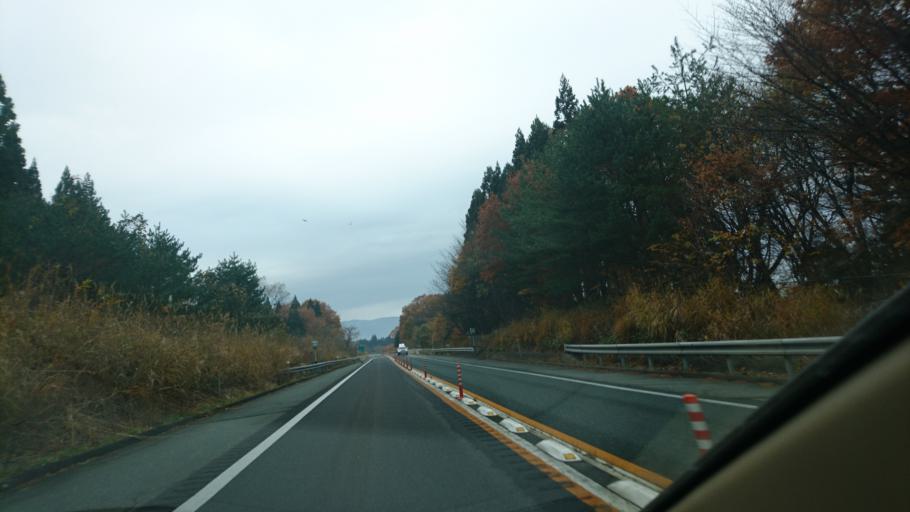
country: JP
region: Iwate
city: Kitakami
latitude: 39.2863
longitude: 140.9944
